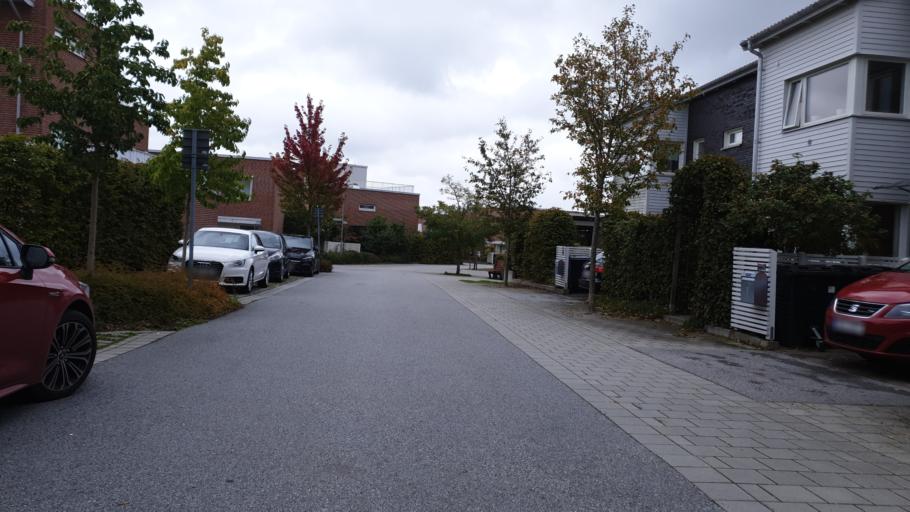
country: SE
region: Skane
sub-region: Lunds Kommun
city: Lund
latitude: 55.7141
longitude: 13.2432
